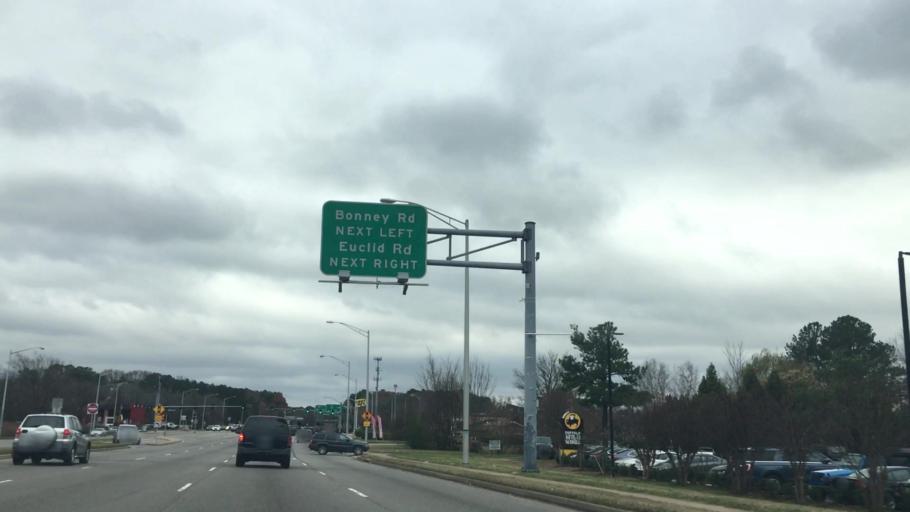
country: US
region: Virginia
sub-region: City of Chesapeake
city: Chesapeake
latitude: 36.8398
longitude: -76.1370
